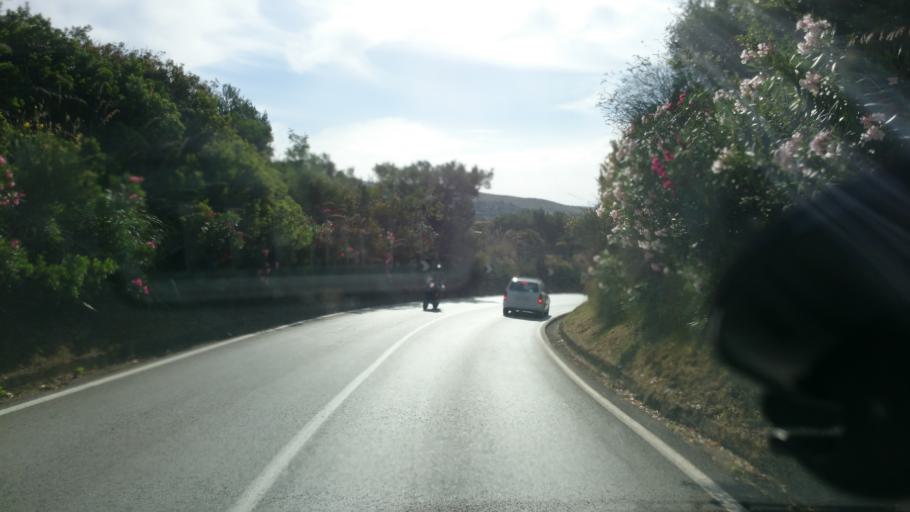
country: IT
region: Campania
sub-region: Provincia di Salerno
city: Marina di Camerota
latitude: 40.0066
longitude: 15.3554
